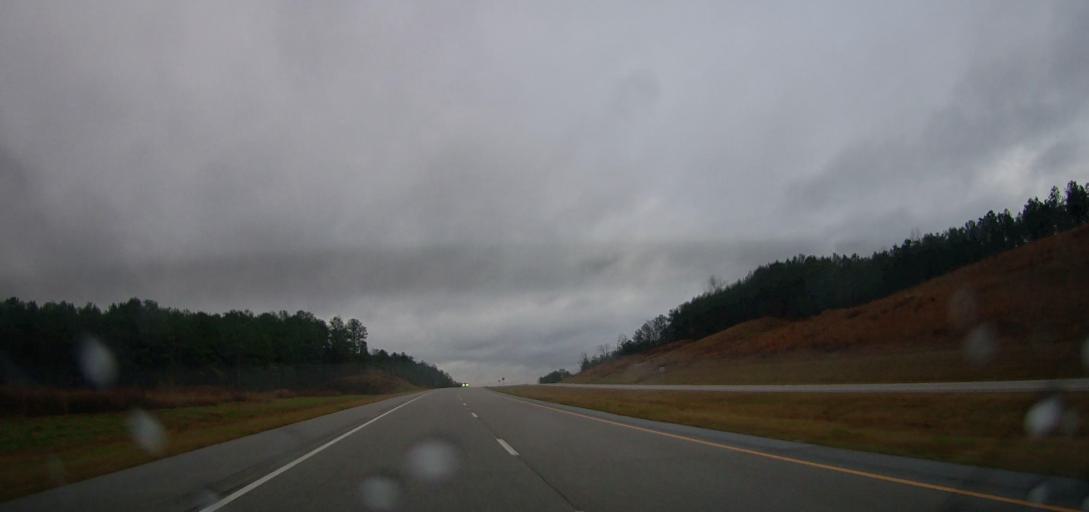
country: US
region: Alabama
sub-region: Bibb County
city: Centreville
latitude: 32.9543
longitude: -87.1149
